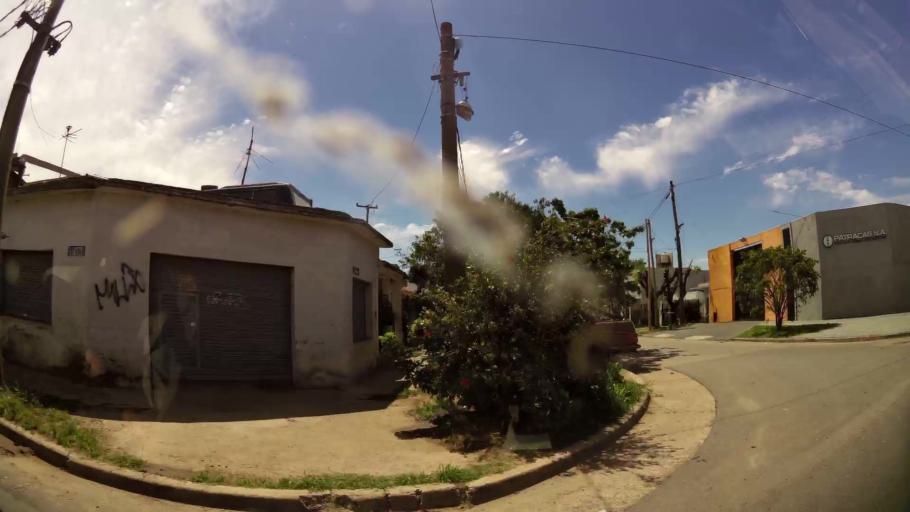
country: AR
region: Buenos Aires
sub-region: Partido de Quilmes
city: Quilmes
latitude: -34.7488
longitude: -58.2964
